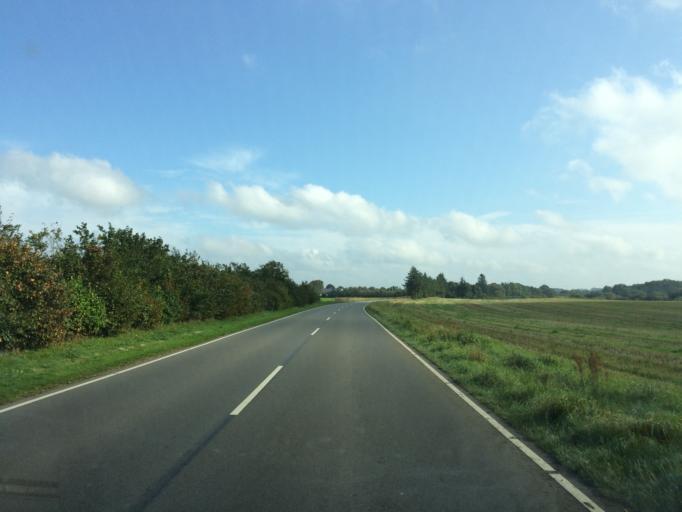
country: DK
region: Central Jutland
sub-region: Skive Kommune
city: Skive
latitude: 56.4704
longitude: 8.9498
